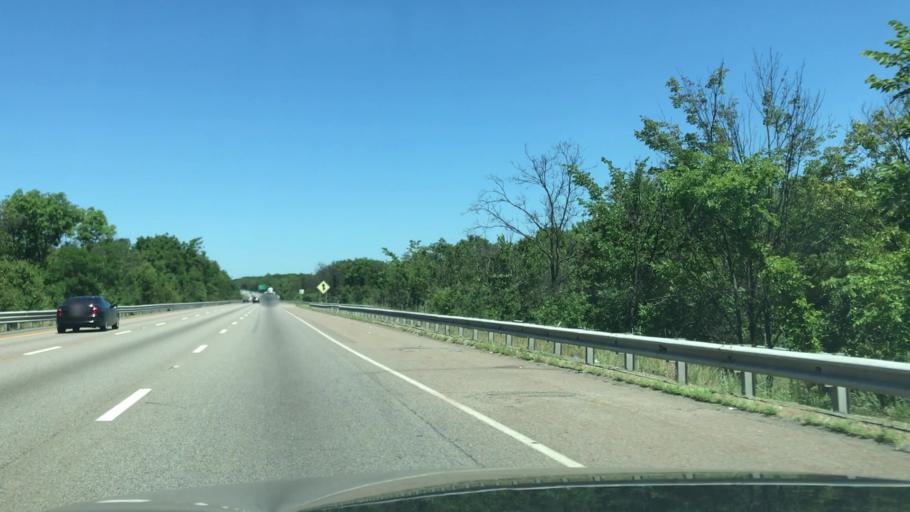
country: US
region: Massachusetts
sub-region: Bristol County
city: Attleboro
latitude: 41.9348
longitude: -71.3183
